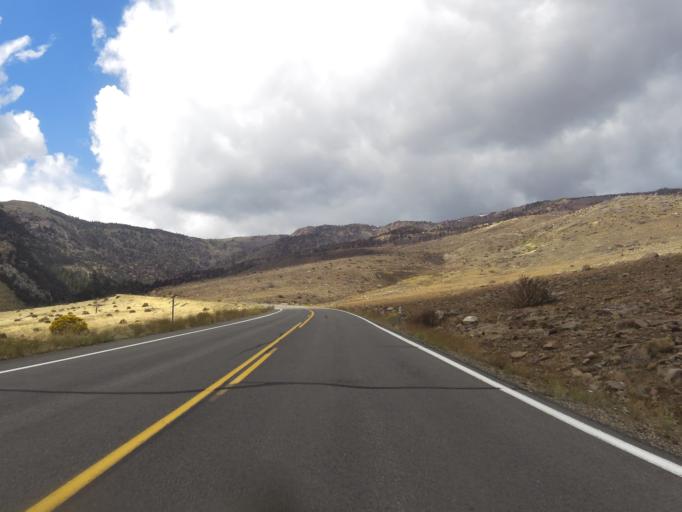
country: US
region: Nevada
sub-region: Lyon County
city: Smith Valley
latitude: 38.6549
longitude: -119.5793
